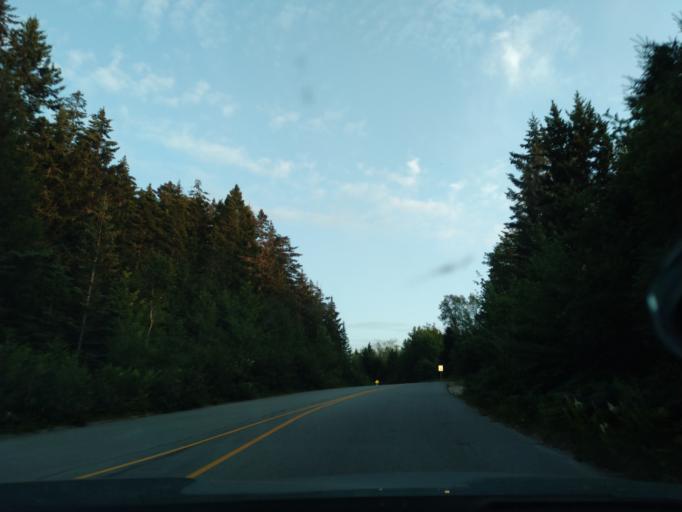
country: US
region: Maine
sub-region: Hancock County
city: Gouldsboro
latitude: 44.3937
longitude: -68.0737
